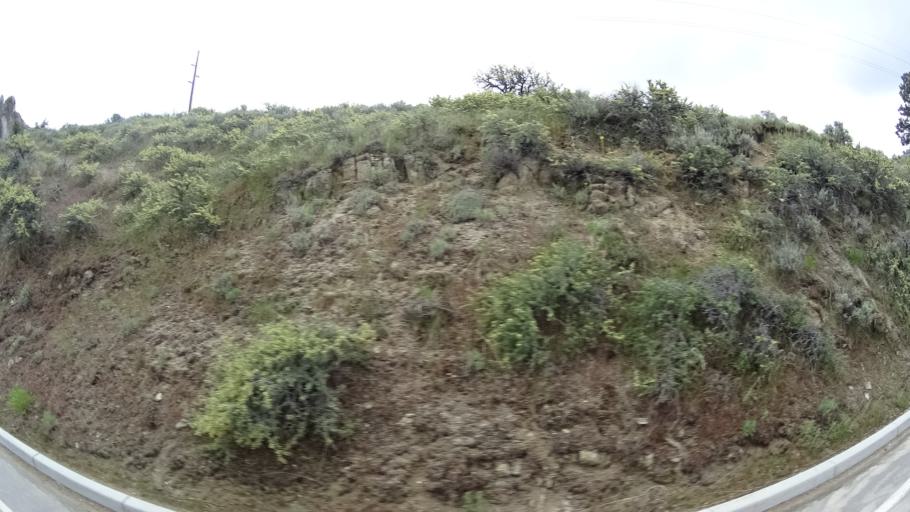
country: US
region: Idaho
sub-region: Ada County
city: Boise
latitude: 43.7247
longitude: -116.1577
